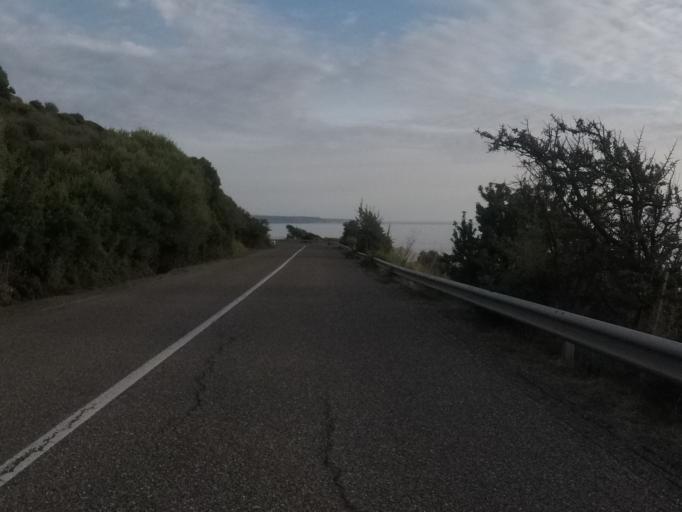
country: IT
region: Sardinia
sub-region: Provincia di Oristano
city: Bosa
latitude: 40.3370
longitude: 8.4298
